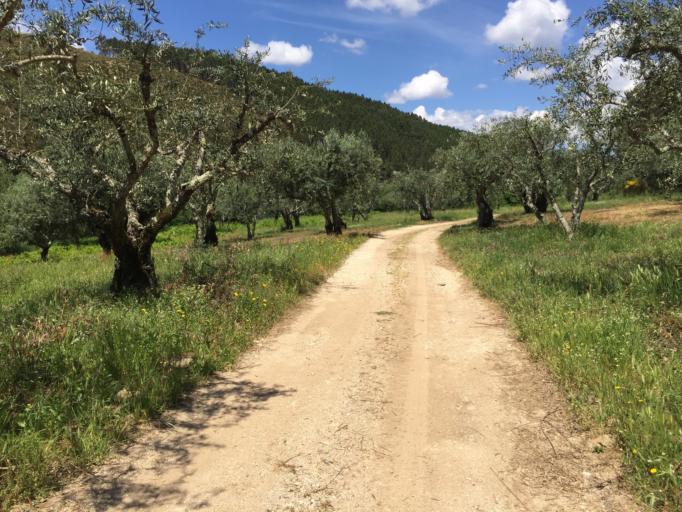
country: PT
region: Coimbra
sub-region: Pampilhosa da Serra
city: Pampilhosa da Serra
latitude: 40.0714
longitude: -7.7831
